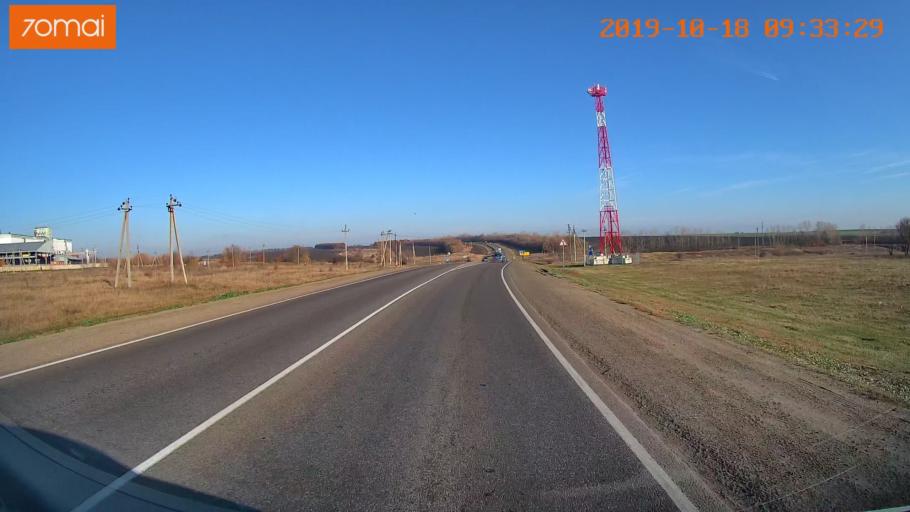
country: RU
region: Tula
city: Yefremov
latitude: 53.1673
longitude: 38.1511
